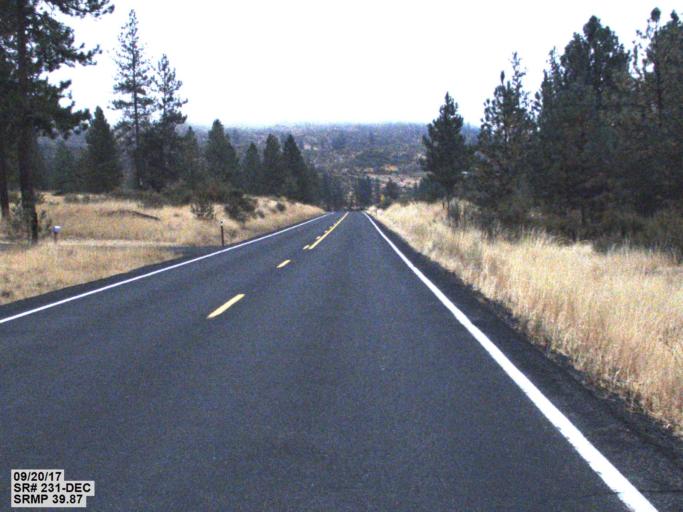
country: US
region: Washington
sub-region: Lincoln County
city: Davenport
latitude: 47.7873
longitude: -117.8897
